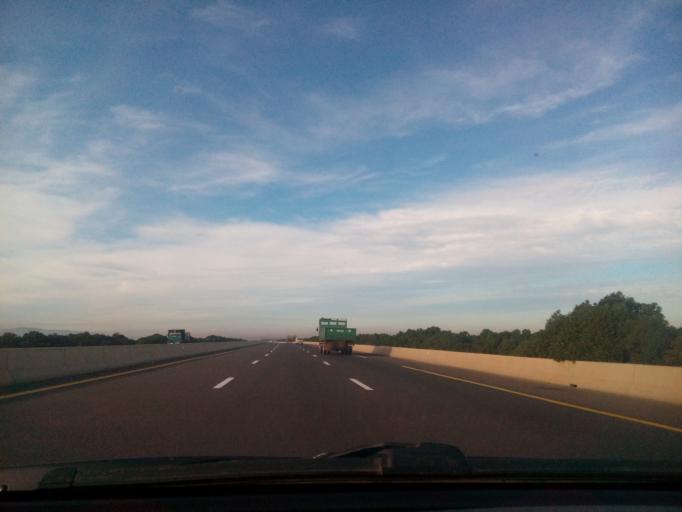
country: DZ
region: Mascara
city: Sig
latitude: 35.5908
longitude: -0.0667
